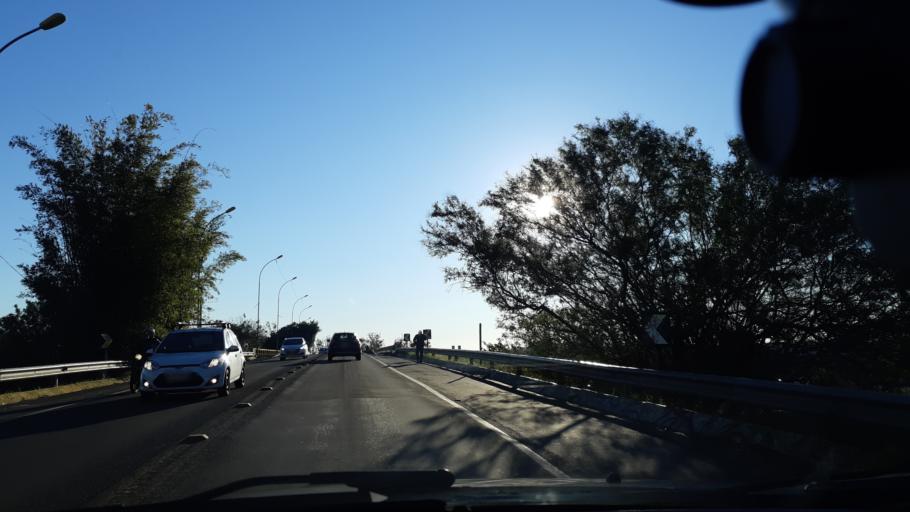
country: BR
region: Rio Grande do Sul
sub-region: Sao Leopoldo
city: Sao Leopoldo
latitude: -29.7608
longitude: -51.1510
